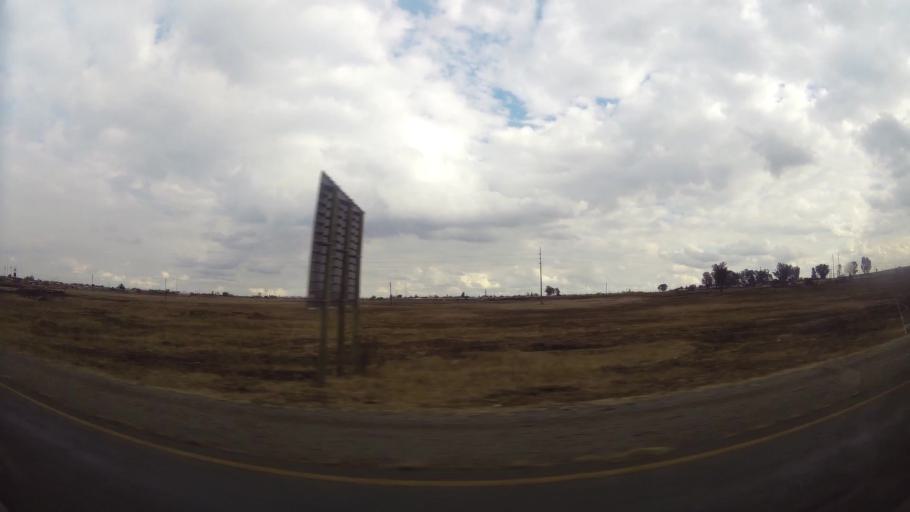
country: ZA
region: Orange Free State
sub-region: Fezile Dabi District Municipality
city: Sasolburg
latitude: -26.8426
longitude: 27.8808
